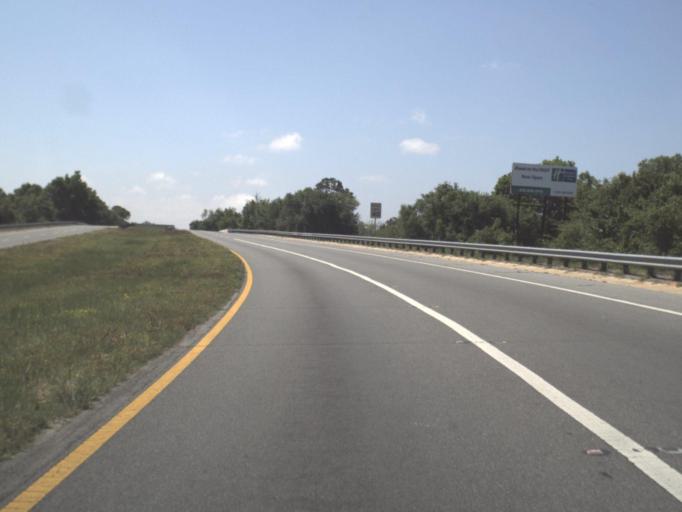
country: US
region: Florida
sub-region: Escambia County
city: West Pensacola
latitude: 30.4286
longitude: -87.2746
